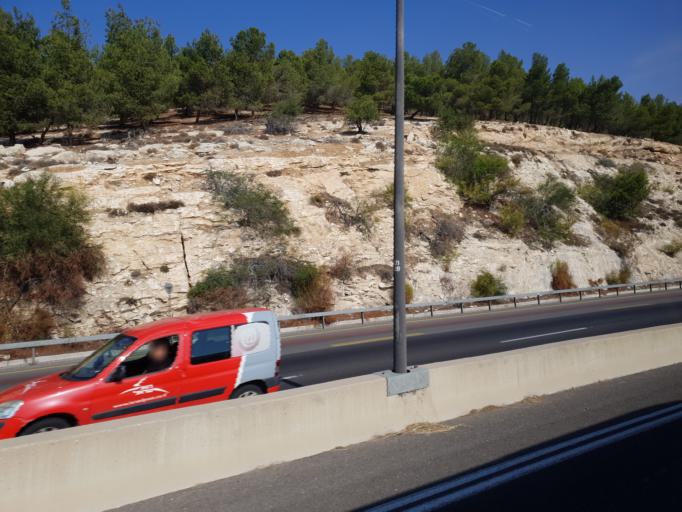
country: PS
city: Az Za`ayyim
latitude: 31.7879
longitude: 35.2747
